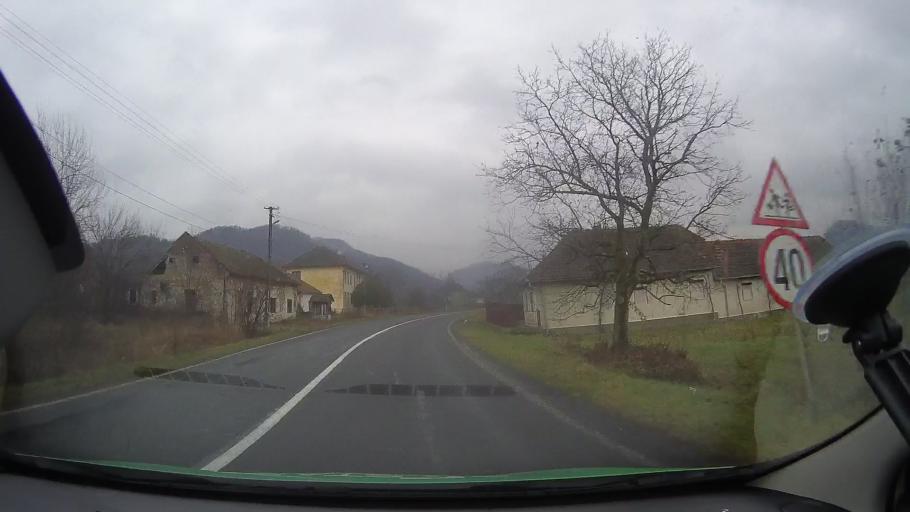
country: RO
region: Arad
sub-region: Comuna Plescuta
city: Plescuta
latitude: 46.2984
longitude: 22.4210
